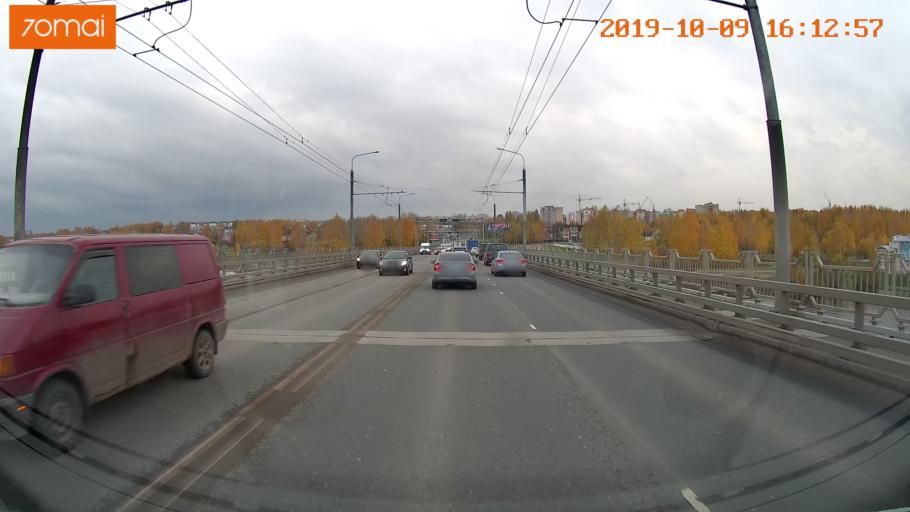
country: RU
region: Kostroma
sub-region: Kostromskoy Rayon
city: Kostroma
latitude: 57.7497
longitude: 40.9343
